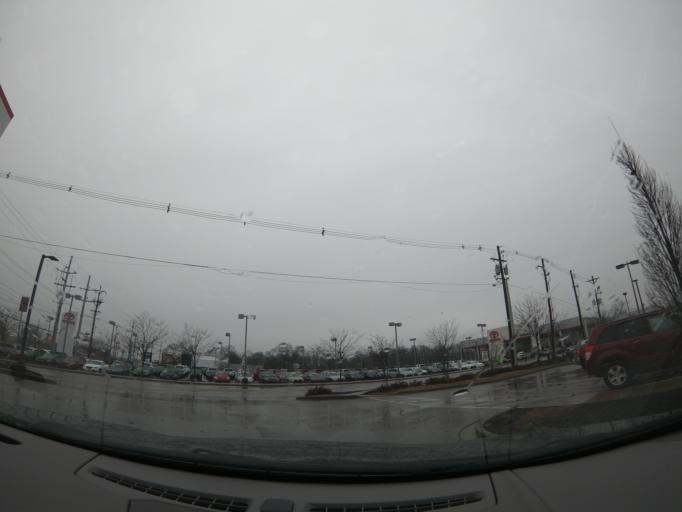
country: US
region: Kentucky
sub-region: Jefferson County
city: Lyndon
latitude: 38.2493
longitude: -85.6050
